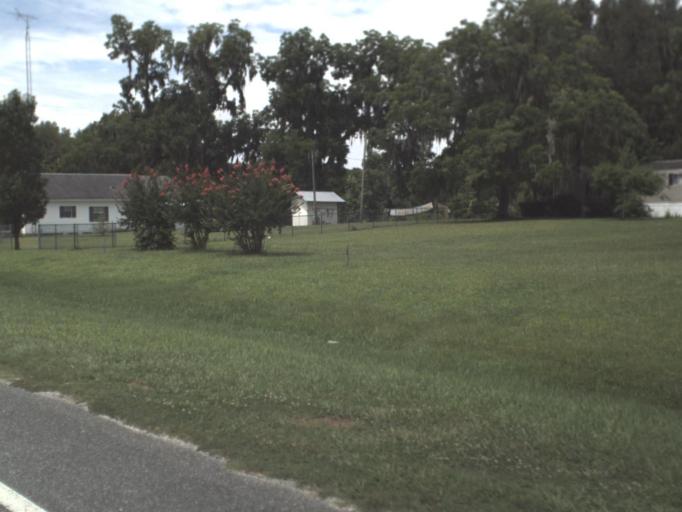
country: US
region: Florida
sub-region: Suwannee County
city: Live Oak
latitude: 30.3607
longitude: -82.9432
